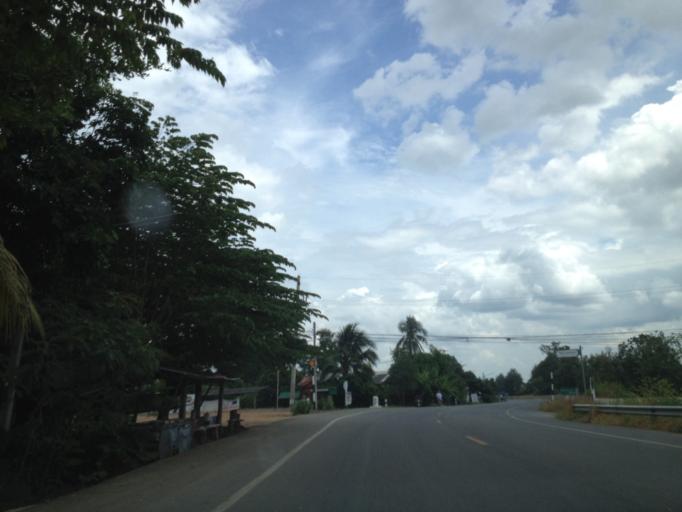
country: TH
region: Chiang Mai
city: San Pa Tong
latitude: 18.6335
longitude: 98.8632
